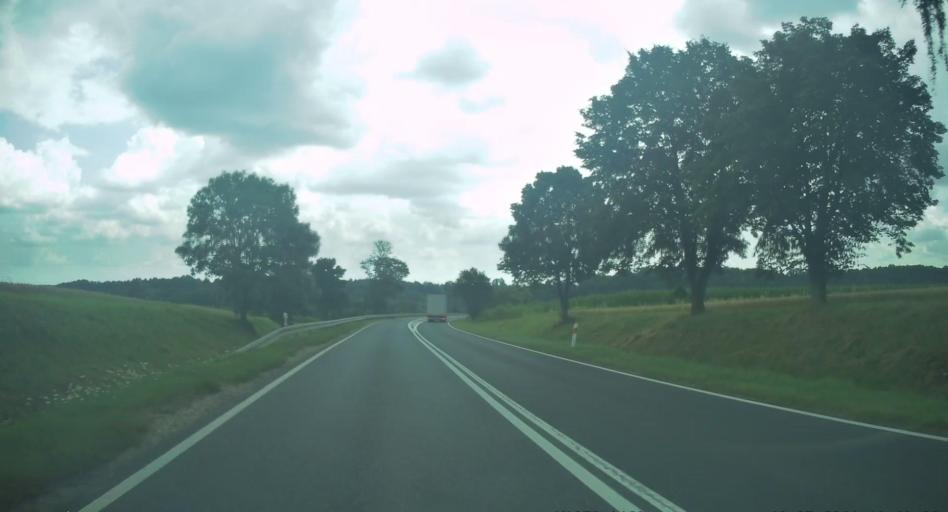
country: PL
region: Opole Voivodeship
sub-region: Powiat prudnicki
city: Laka Prudnicka
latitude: 50.4092
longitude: 17.5064
